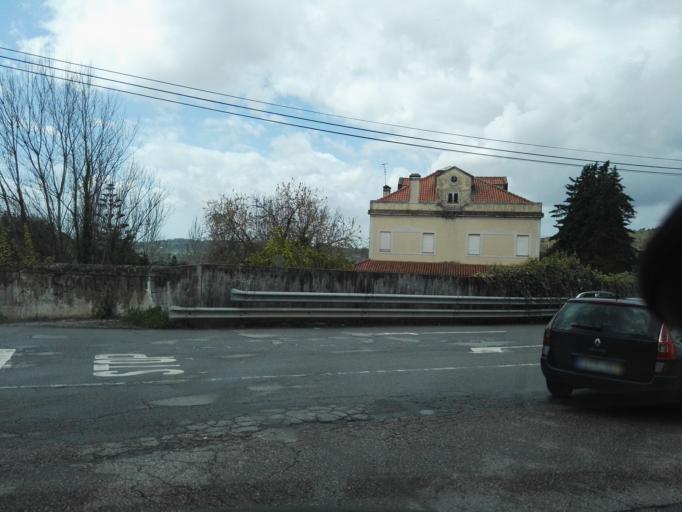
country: PT
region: Portalegre
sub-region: Portalegre
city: Portalegre
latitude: 39.2967
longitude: -7.4327
